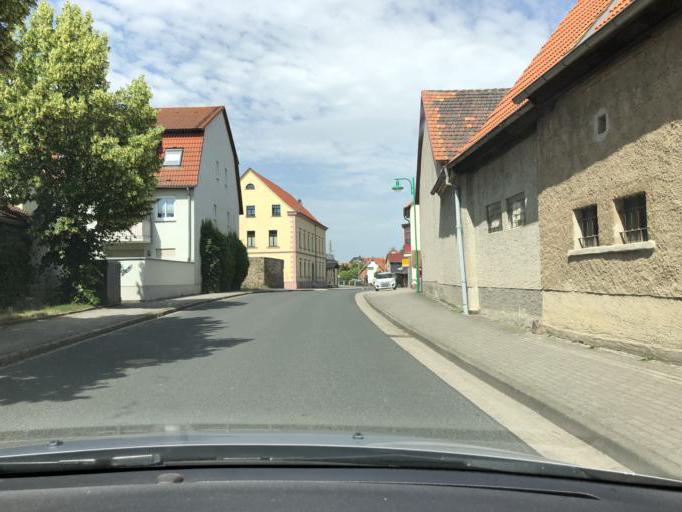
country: DE
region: Saxony
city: Borsdorf
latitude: 51.3349
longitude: 12.5482
